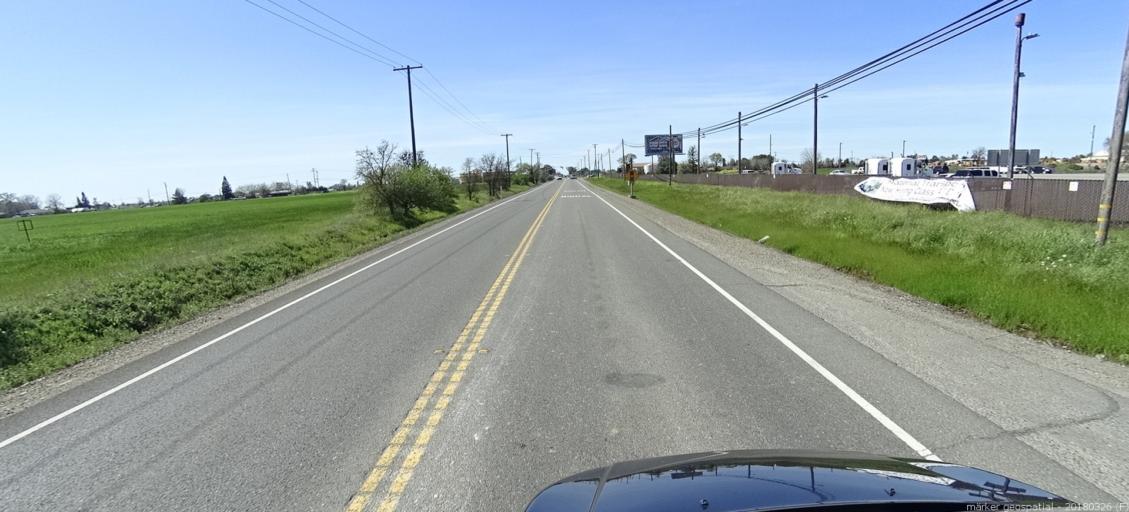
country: US
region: California
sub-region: Sacramento County
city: Rosemont
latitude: 38.5279
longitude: -121.3309
